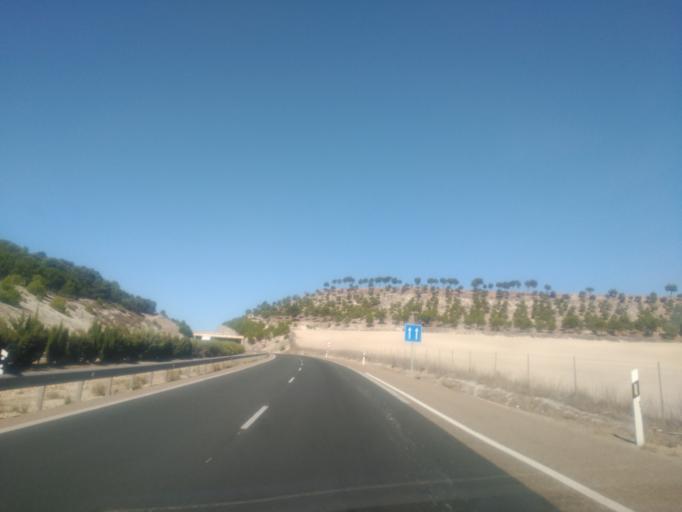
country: ES
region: Castille and Leon
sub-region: Provincia de Valladolid
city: Cisterniga
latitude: 41.6065
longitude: -4.6647
